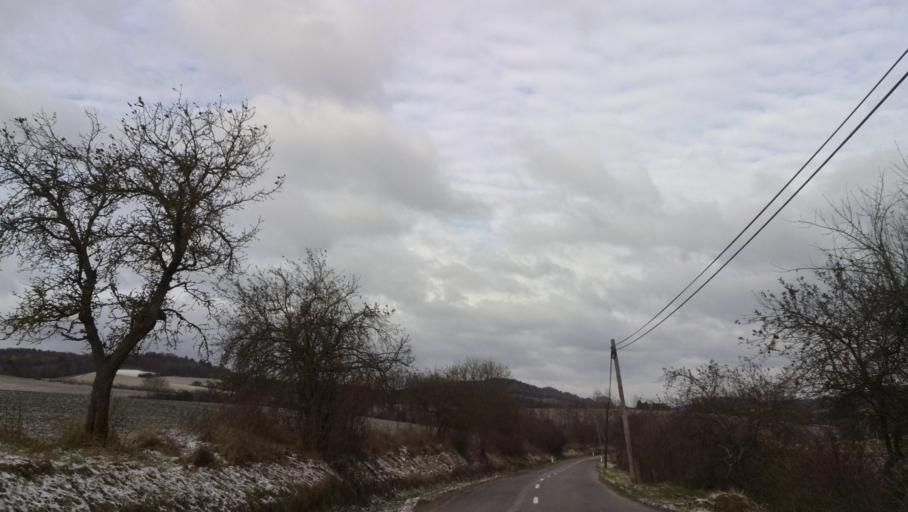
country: SK
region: Presovsky
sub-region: Okres Presov
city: Presov
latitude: 48.9178
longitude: 21.1948
